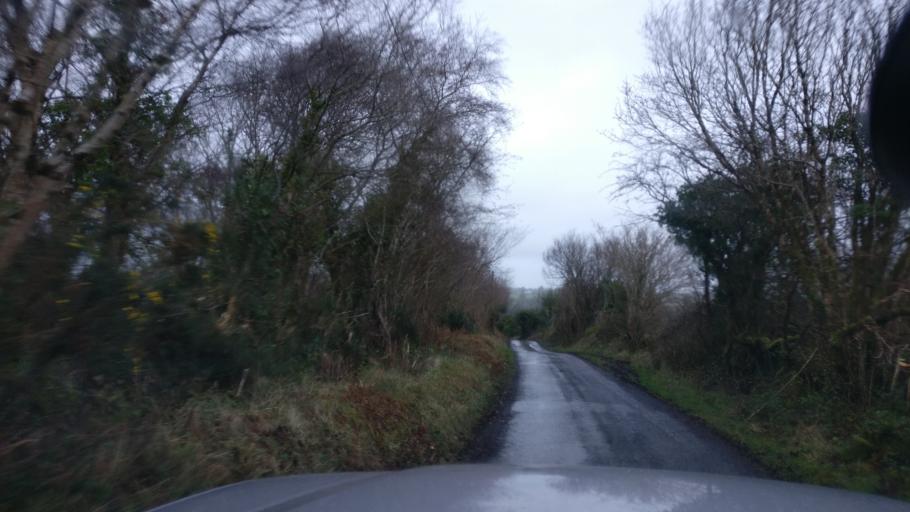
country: IE
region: Connaught
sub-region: County Galway
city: Loughrea
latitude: 53.1500
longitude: -8.6139
